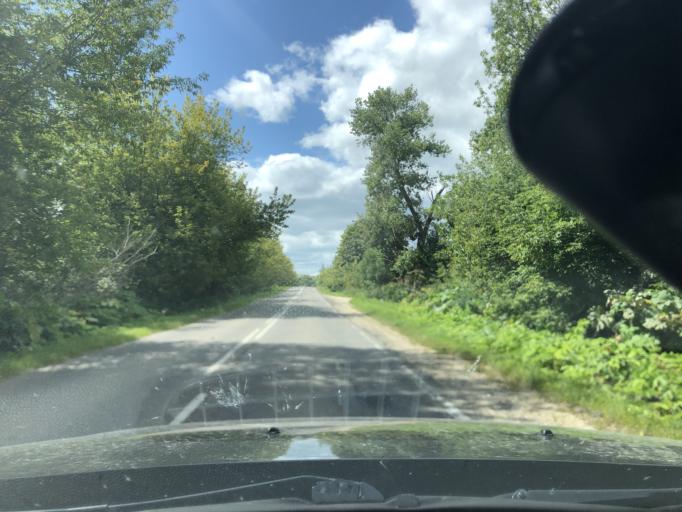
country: RU
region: Tula
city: Revyakino
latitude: 54.3440
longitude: 37.5944
